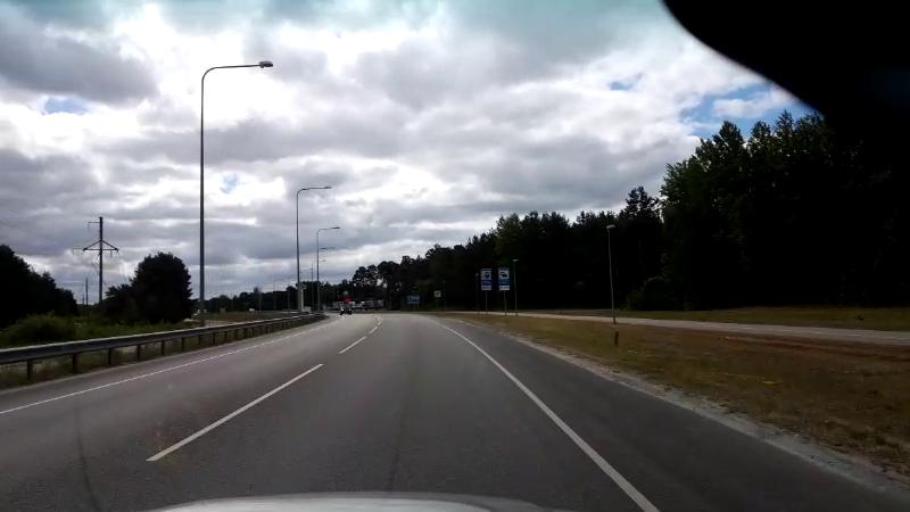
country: EE
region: Paernumaa
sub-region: Paernu linn
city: Parnu
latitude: 58.3640
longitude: 24.5614
